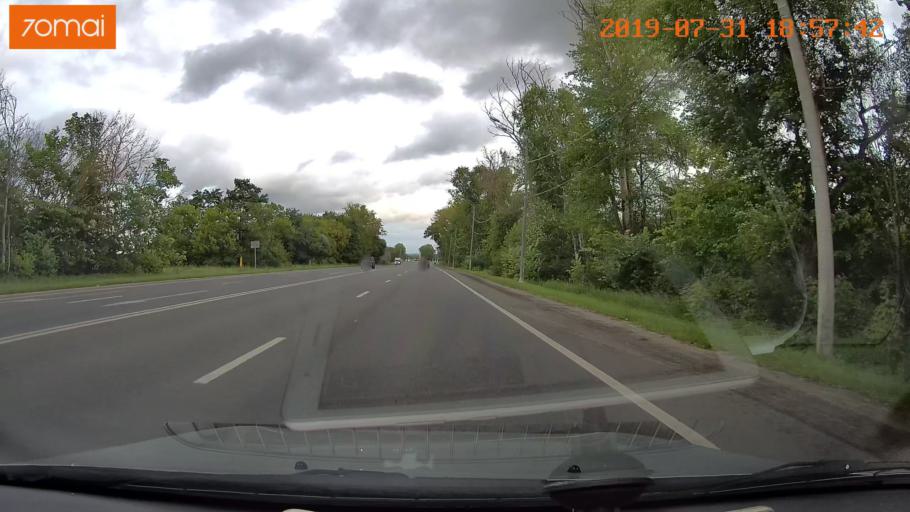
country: RU
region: Moskovskaya
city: Raduzhnyy
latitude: 55.1521
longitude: 38.6955
